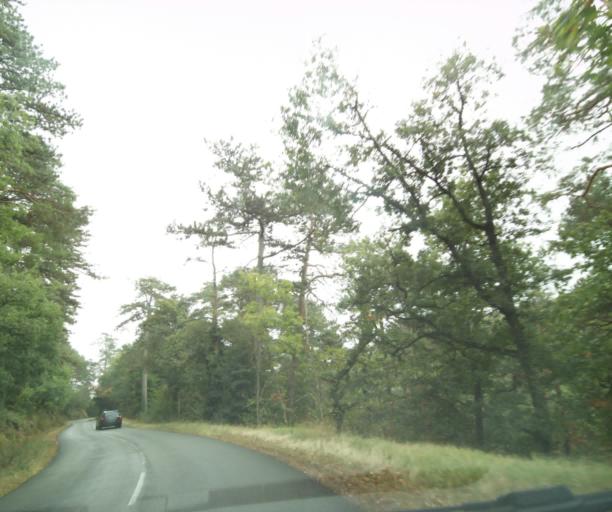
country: FR
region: Auvergne
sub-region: Departement du Puy-de-Dome
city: Durtol
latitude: 45.7948
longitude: 3.0327
